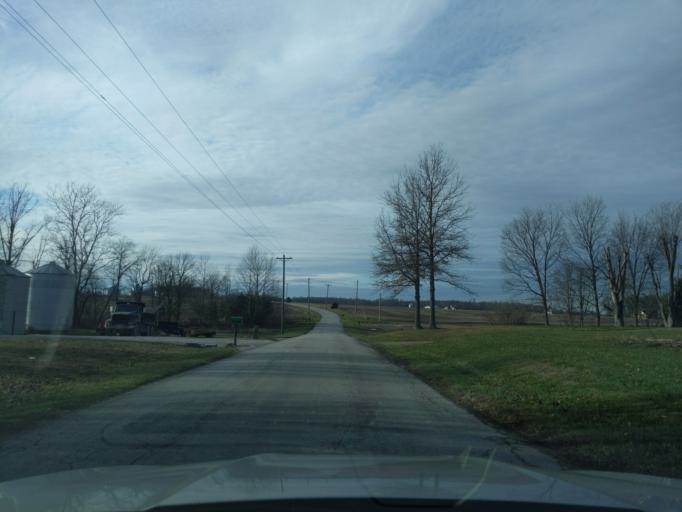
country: US
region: Indiana
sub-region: Decatur County
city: Westport
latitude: 39.2163
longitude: -85.4587
